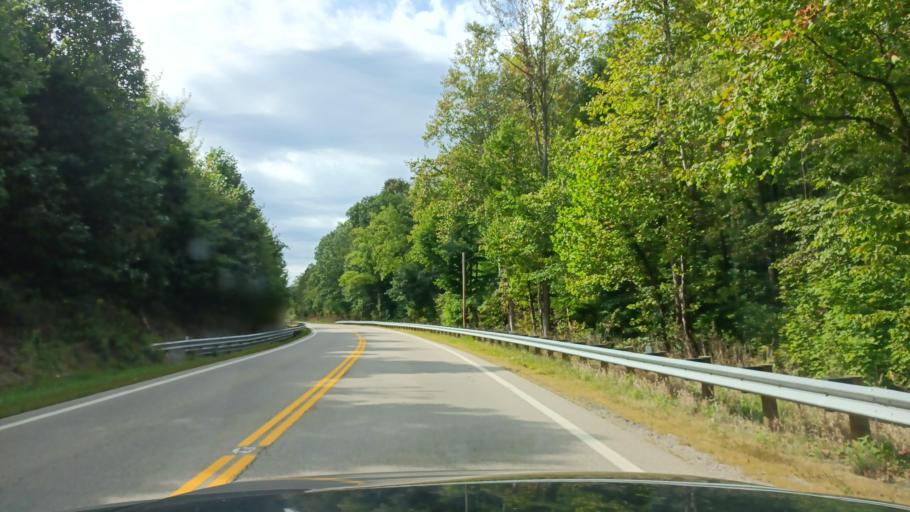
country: US
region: Ohio
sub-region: Vinton County
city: McArthur
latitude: 39.2406
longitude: -82.3529
